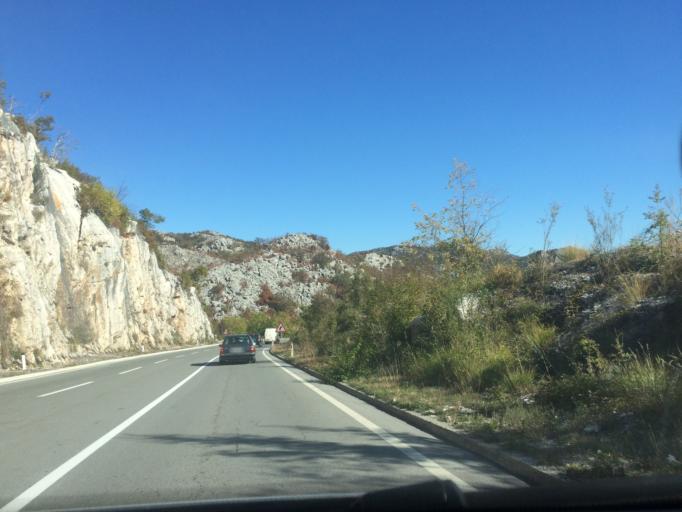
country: ME
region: Cetinje
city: Cetinje
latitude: 42.3770
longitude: 18.9803
